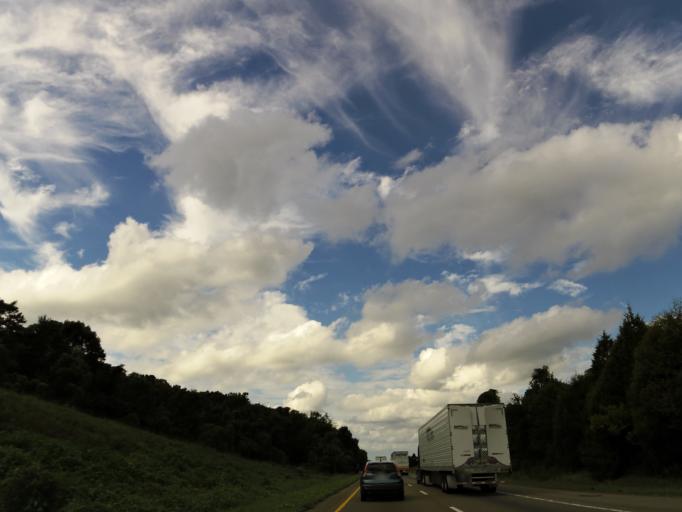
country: US
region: Tennessee
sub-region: Loudon County
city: Lenoir City
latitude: 35.7980
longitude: -84.3201
